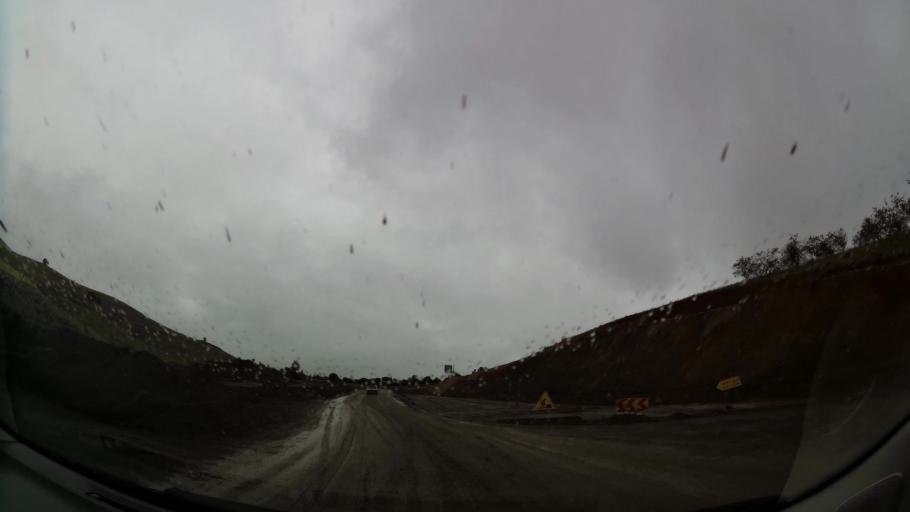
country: MA
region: Taza-Al Hoceima-Taounate
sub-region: Taza
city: Ajdir
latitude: 34.9034
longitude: -3.7926
